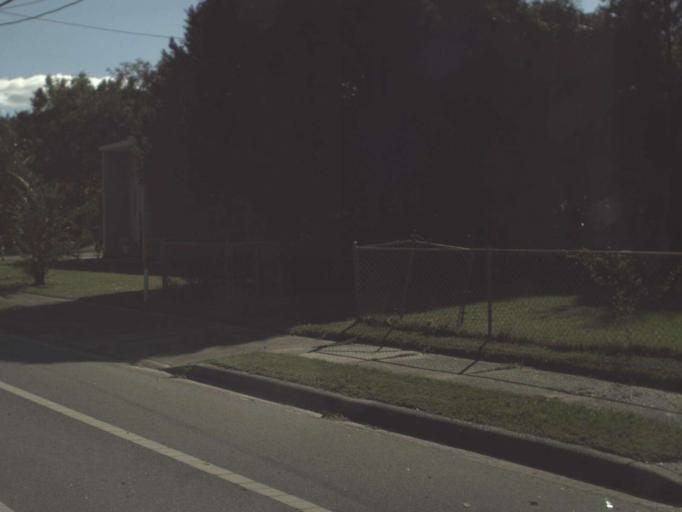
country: US
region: Florida
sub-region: Gulf County
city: Wewahitchka
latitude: 30.1040
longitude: -85.2007
